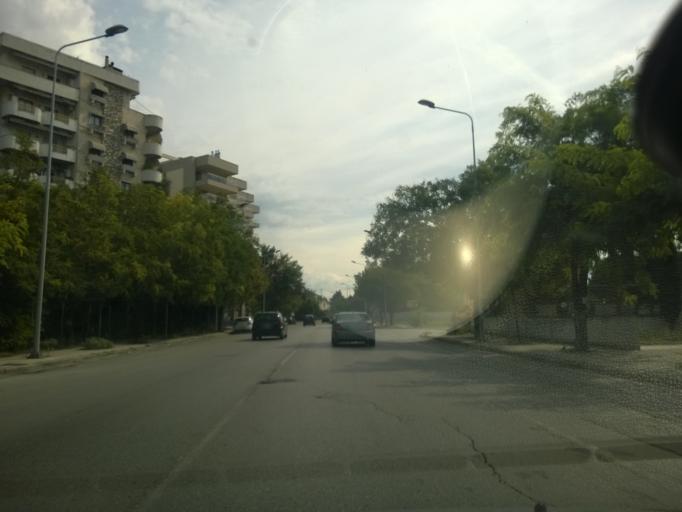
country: GR
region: Central Macedonia
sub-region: Nomos Thessalonikis
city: Kalamaria
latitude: 40.5825
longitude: 22.9640
